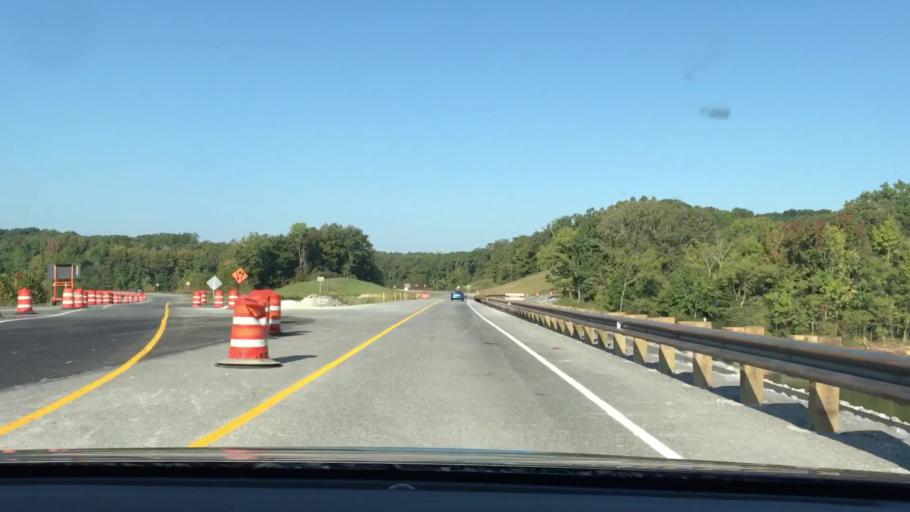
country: US
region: Kentucky
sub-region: Trigg County
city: Cadiz
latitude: 36.8020
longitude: -87.9840
